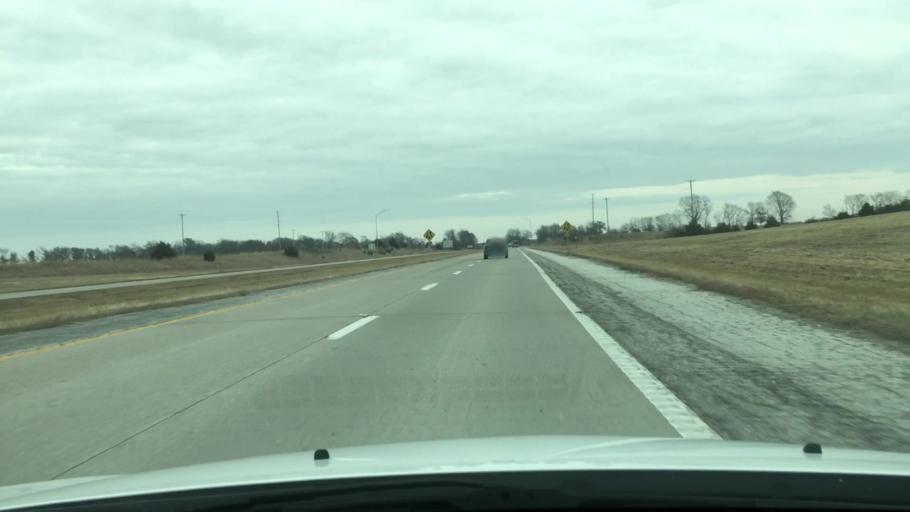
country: US
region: Missouri
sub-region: Audrain County
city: Mexico
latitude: 39.1175
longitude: -91.8904
